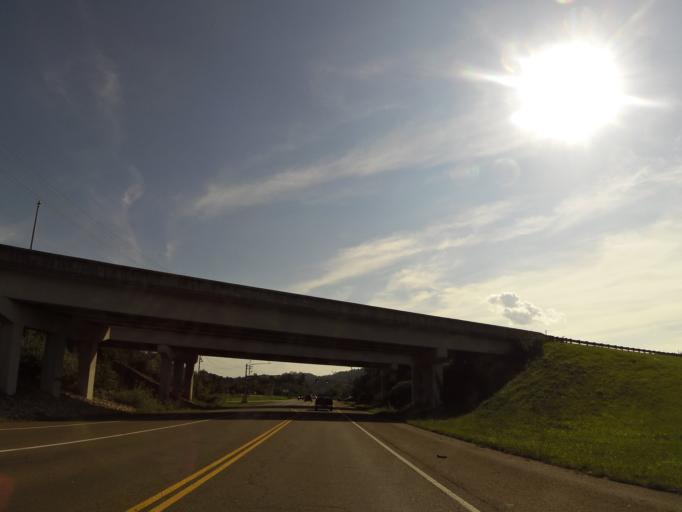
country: US
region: Tennessee
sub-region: Blount County
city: Alcoa
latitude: 35.8464
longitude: -83.9923
